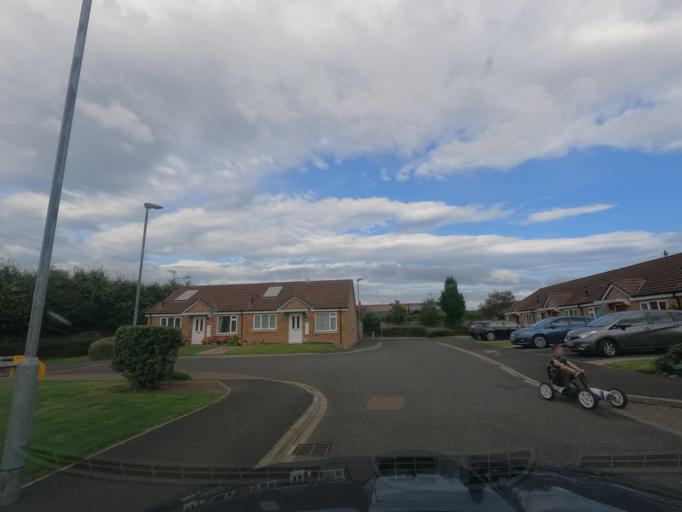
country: GB
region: Scotland
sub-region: The Scottish Borders
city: Allanton
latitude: 55.7187
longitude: -2.1655
